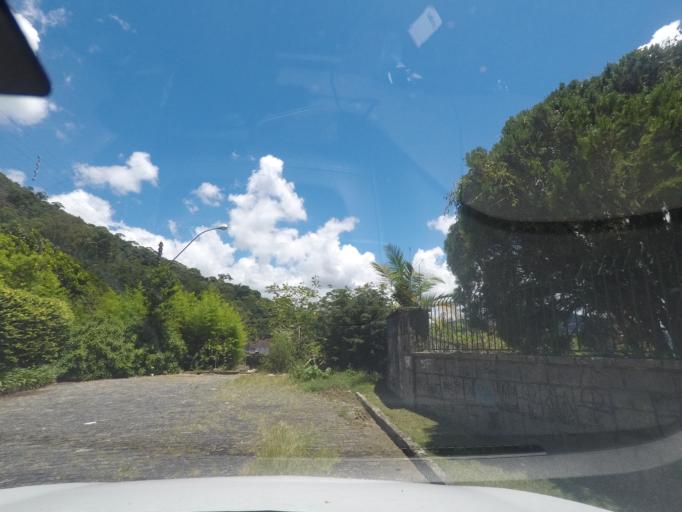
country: BR
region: Rio de Janeiro
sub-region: Teresopolis
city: Teresopolis
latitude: -22.4324
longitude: -42.9821
